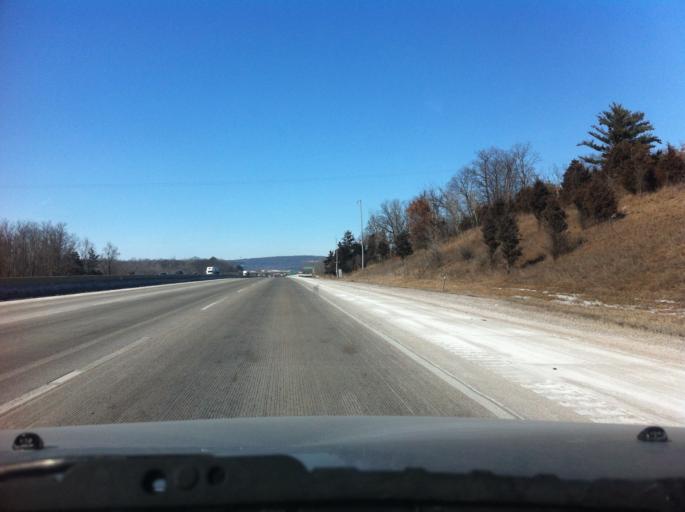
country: US
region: Wisconsin
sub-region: Columbia County
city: Poynette
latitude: 43.4241
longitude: -89.4774
